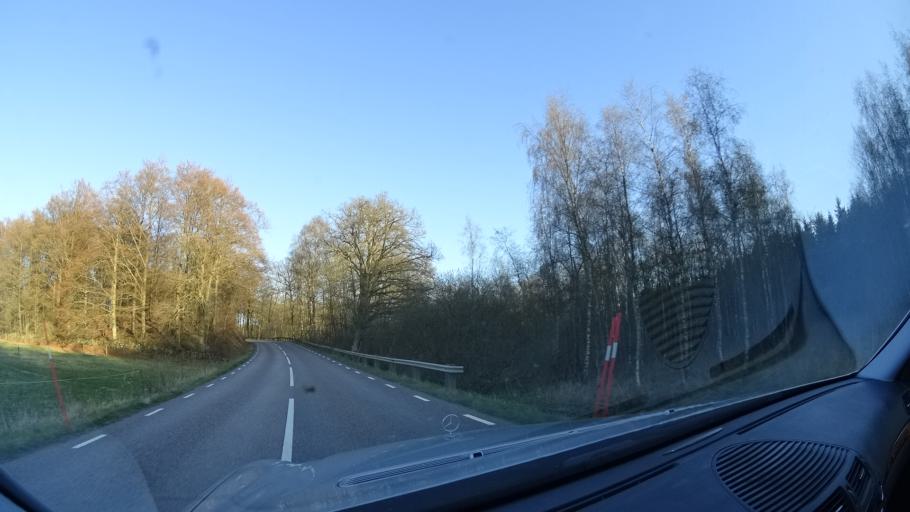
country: SE
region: Skane
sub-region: Svalovs Kommun
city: Kagerod
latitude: 55.9888
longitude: 13.1034
